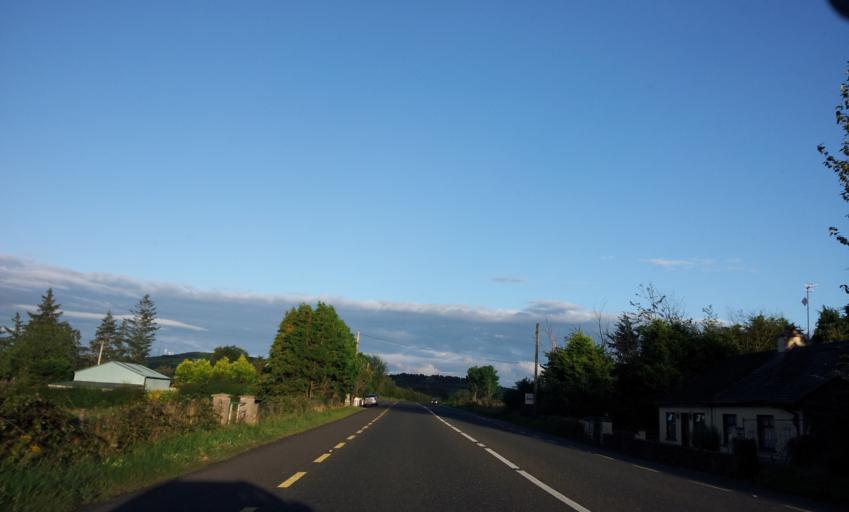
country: IE
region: Munster
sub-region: County Limerick
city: Abbeyfeale
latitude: 52.3864
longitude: -9.2347
